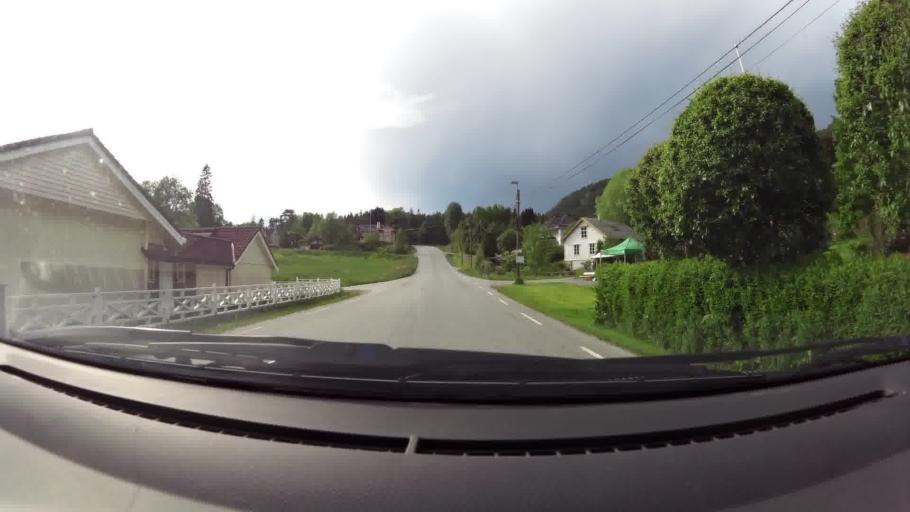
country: NO
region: More og Romsdal
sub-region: Kristiansund
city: Kristiansund
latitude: 63.0293
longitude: 7.7525
